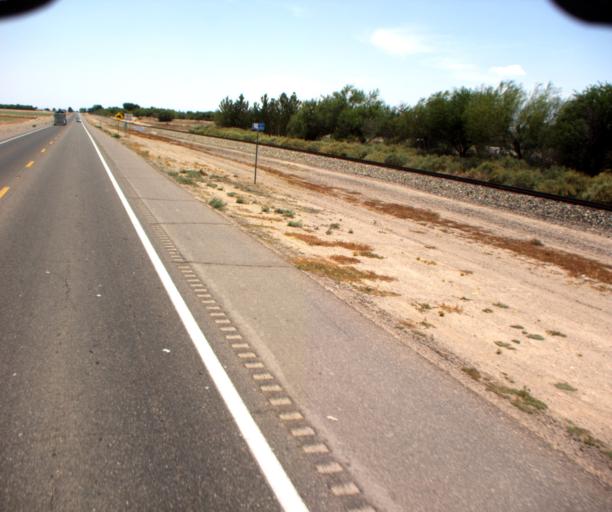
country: US
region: Arizona
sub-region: Graham County
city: Pima
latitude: 32.9098
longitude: -109.8518
